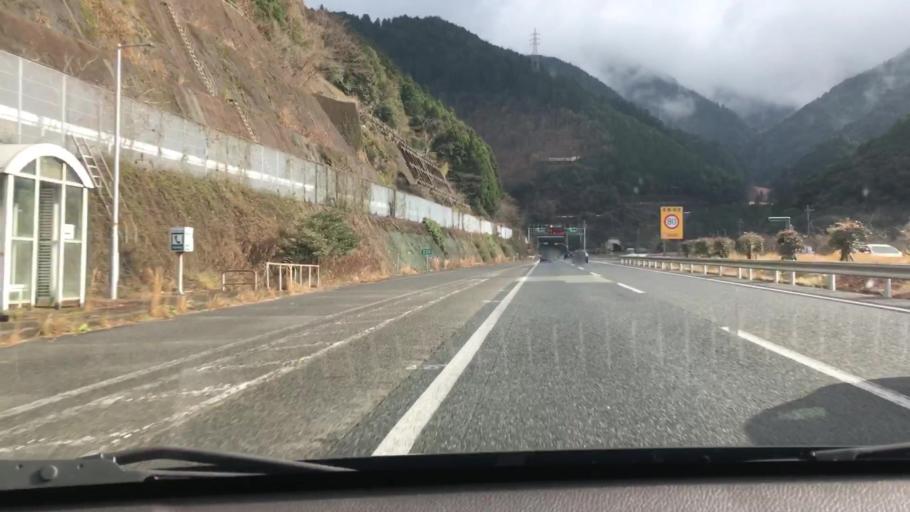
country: JP
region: Kumamoto
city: Yatsushiro
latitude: 32.3968
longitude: 130.7039
